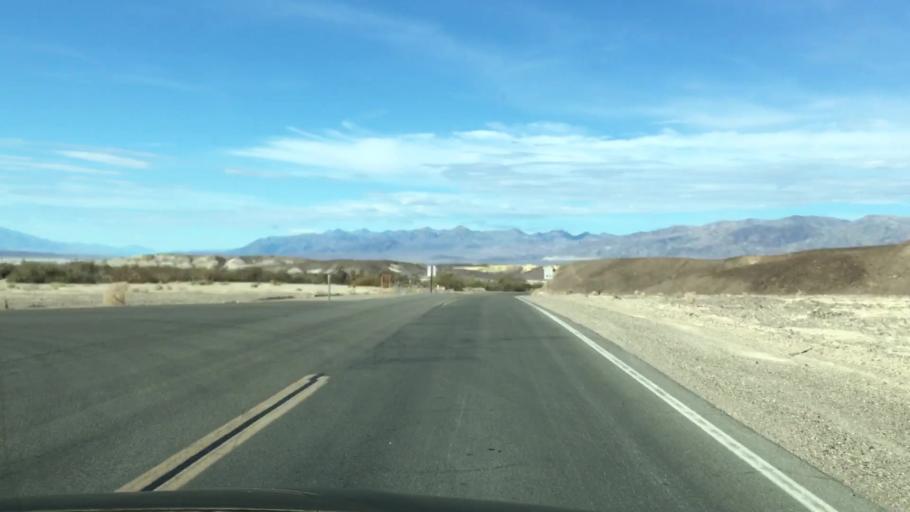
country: US
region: Nevada
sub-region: Nye County
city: Beatty
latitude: 36.4662
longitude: -116.8662
